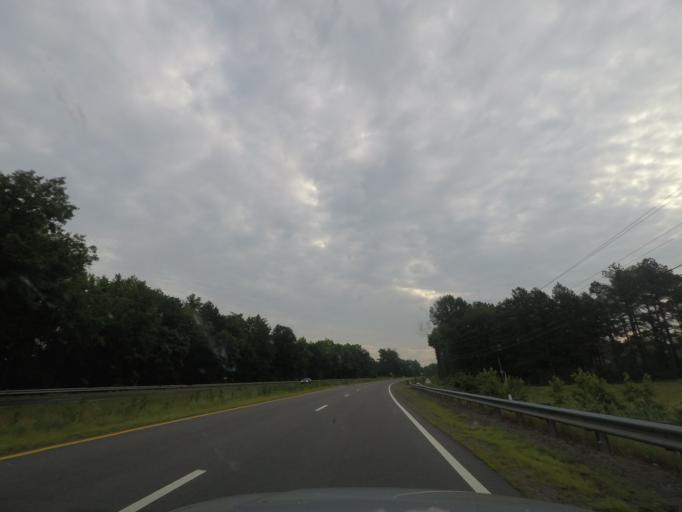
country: US
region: Virginia
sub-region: Halifax County
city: Halifax
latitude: 36.8120
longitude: -78.7522
